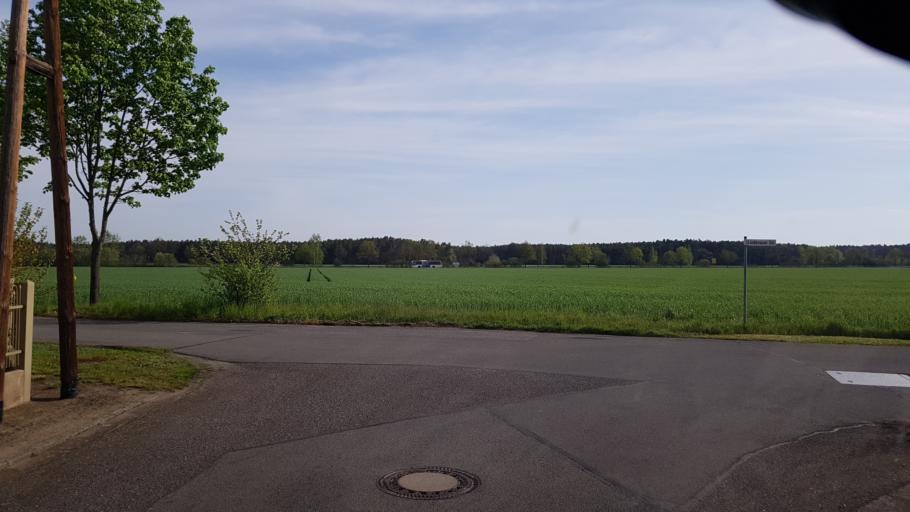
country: DE
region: Brandenburg
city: Ortrand
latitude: 51.3816
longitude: 13.7532
